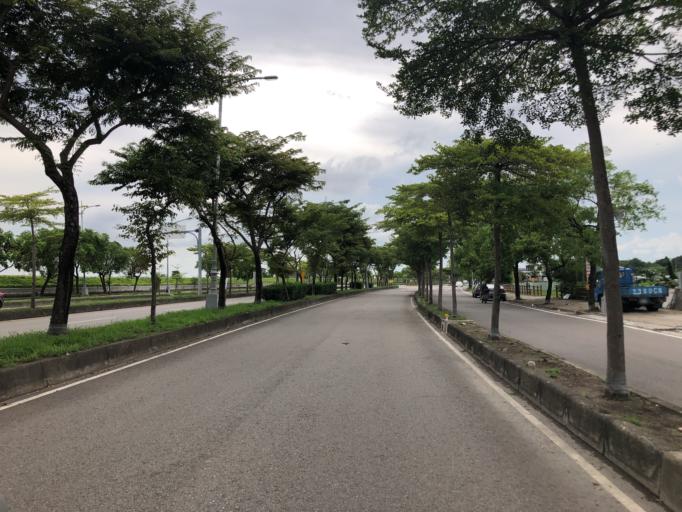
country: TW
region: Taiwan
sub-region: Taichung City
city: Taichung
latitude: 24.0834
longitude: 120.6629
